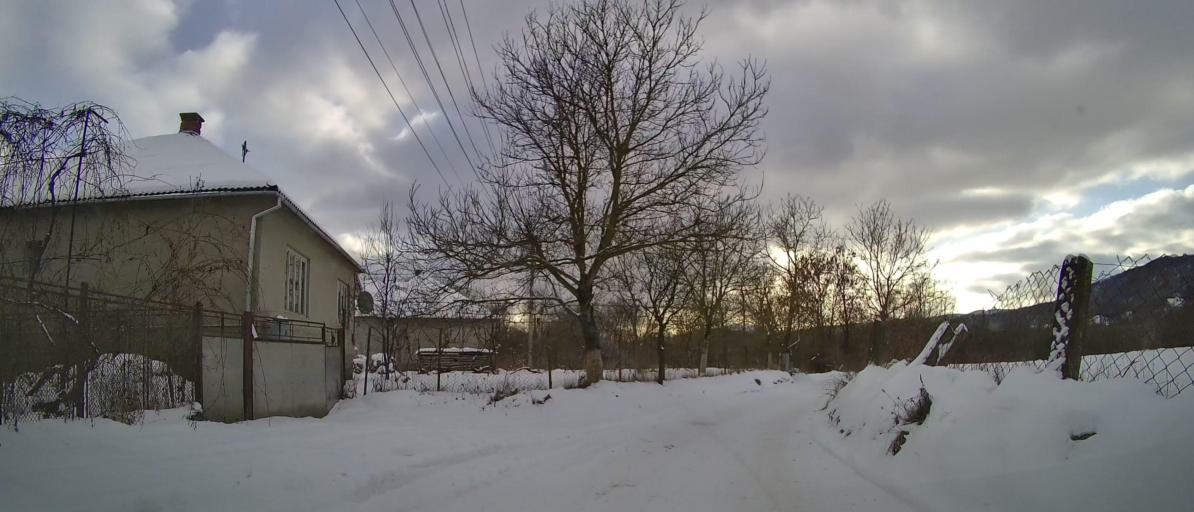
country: UA
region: Zakarpattia
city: Velykyi Bereznyi
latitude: 48.9126
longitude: 22.4647
